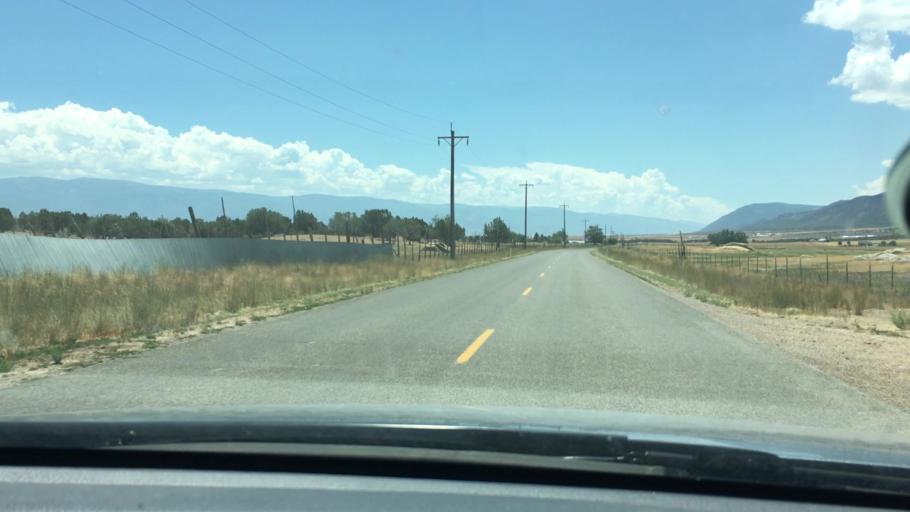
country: US
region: Utah
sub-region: Sanpete County
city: Fountain Green
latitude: 39.6086
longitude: -111.6442
